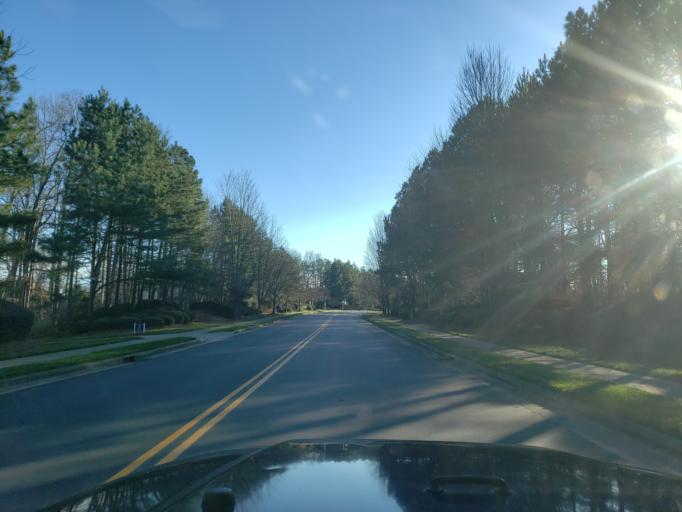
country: US
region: North Carolina
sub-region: Lincoln County
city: Westport
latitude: 35.5300
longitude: -80.9232
